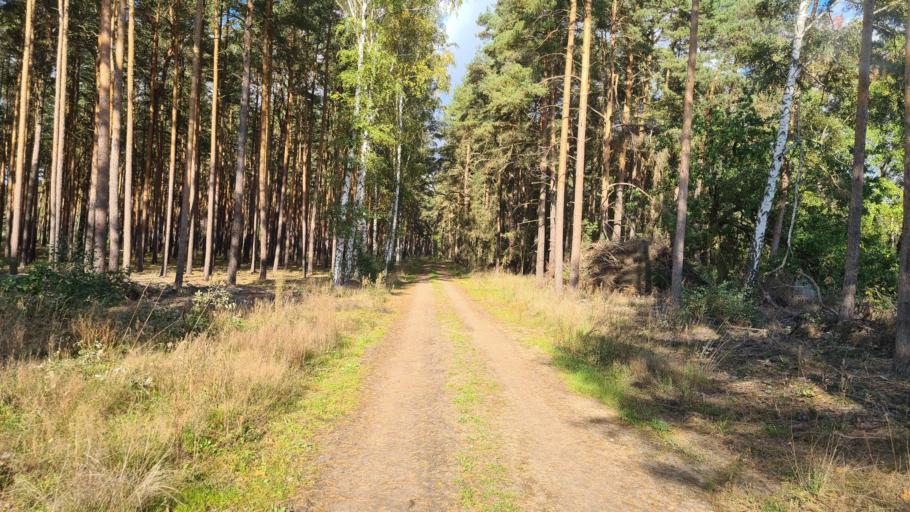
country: DE
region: Brandenburg
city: Vetschau
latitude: 51.7199
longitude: 14.0877
